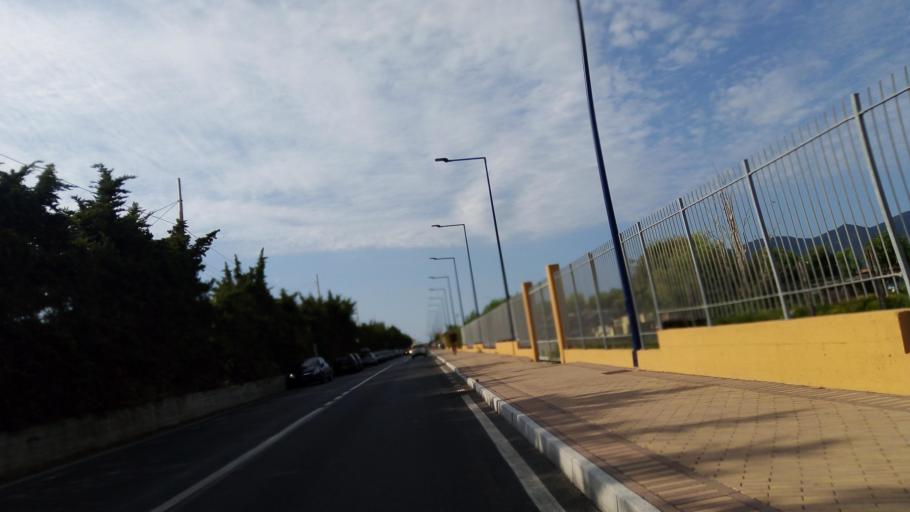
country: IT
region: Liguria
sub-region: Provincia di Savona
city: Ceriale
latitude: 44.0766
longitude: 8.2261
